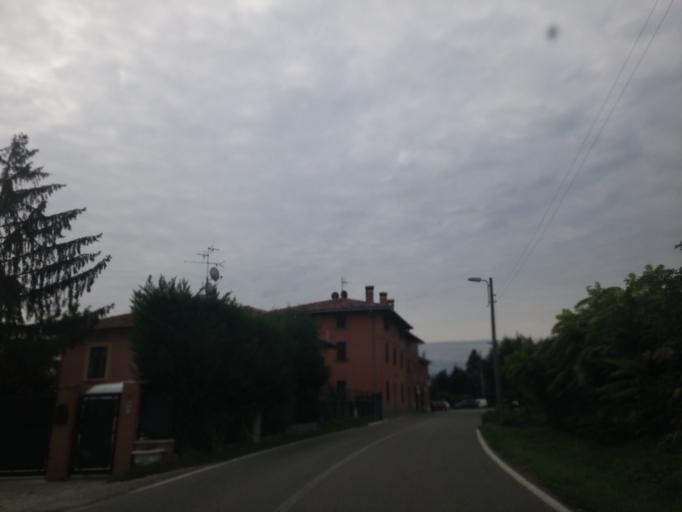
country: IT
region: Emilia-Romagna
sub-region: Provincia di Bologna
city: Longara
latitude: 44.5964
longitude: 11.3225
